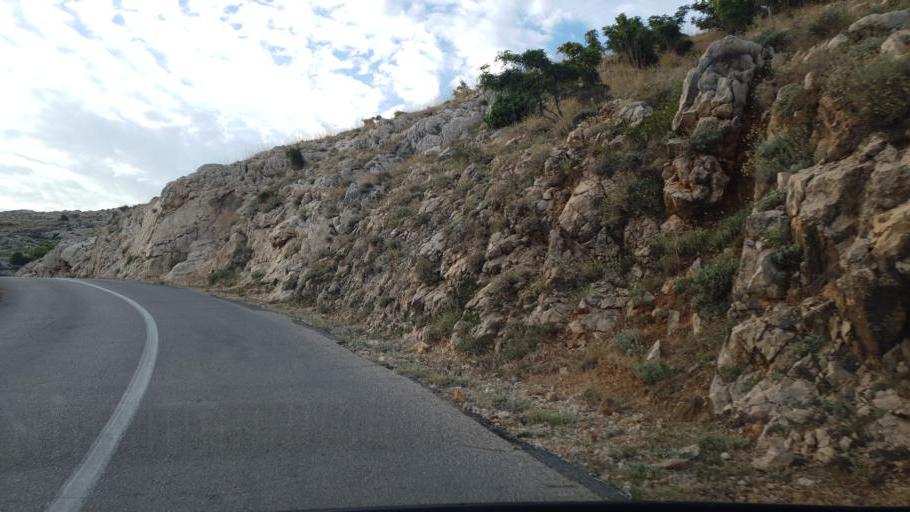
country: HR
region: Primorsko-Goranska
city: Punat
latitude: 44.9739
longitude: 14.6598
